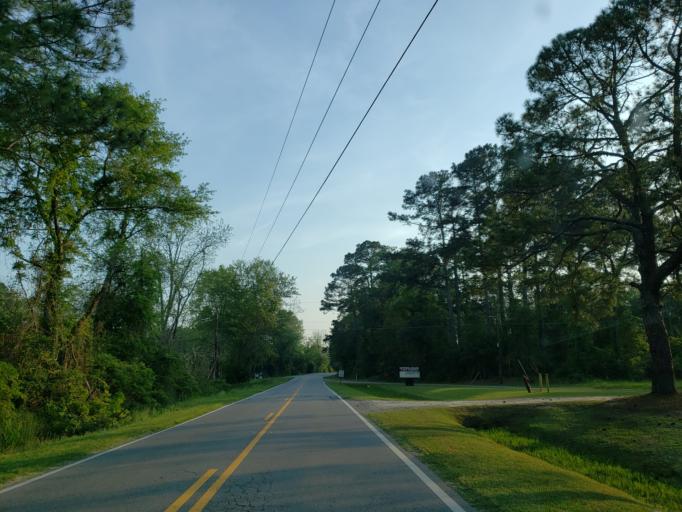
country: US
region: Georgia
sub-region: Cook County
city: Sparks
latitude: 31.1695
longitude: -83.4336
